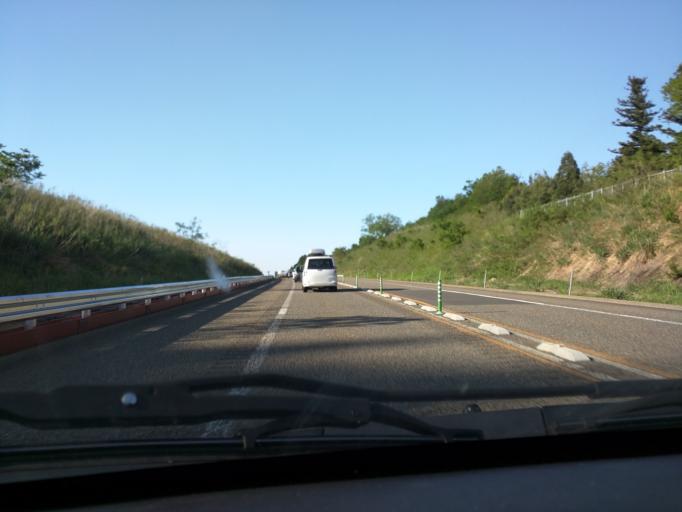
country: JP
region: Niigata
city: Arai
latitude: 37.0341
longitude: 138.2305
